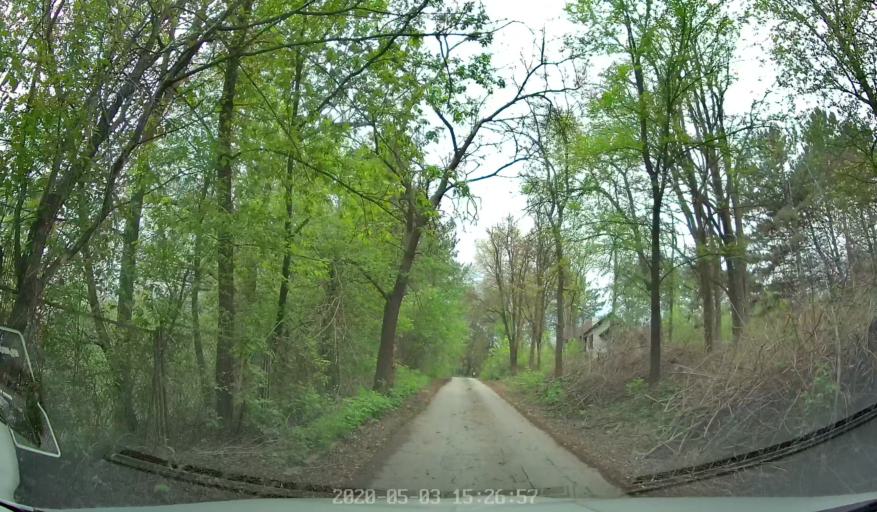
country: MD
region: Chisinau
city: Vatra
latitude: 47.0918
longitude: 28.7113
